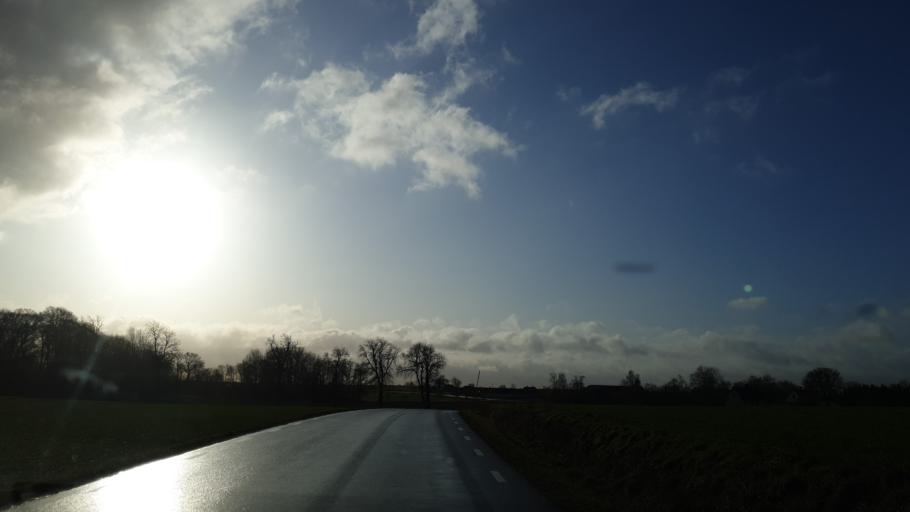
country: SE
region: Skane
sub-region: Skurups Kommun
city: Rydsgard
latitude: 55.4532
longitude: 13.5503
